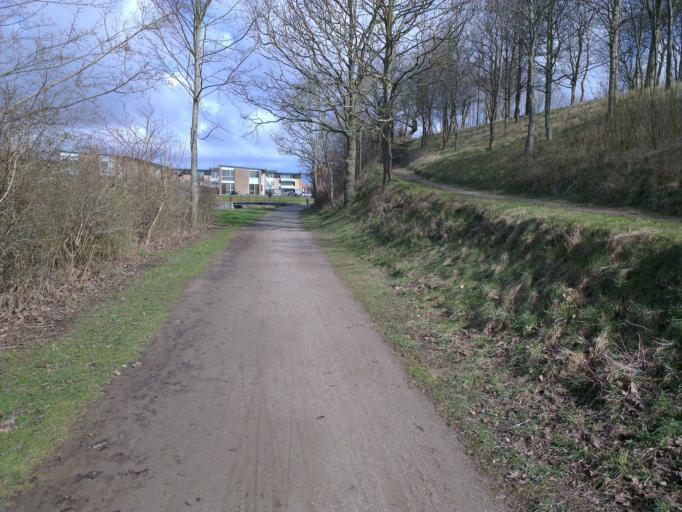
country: DK
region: Capital Region
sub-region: Frederikssund Kommune
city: Frederikssund
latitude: 55.8331
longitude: 12.0563
